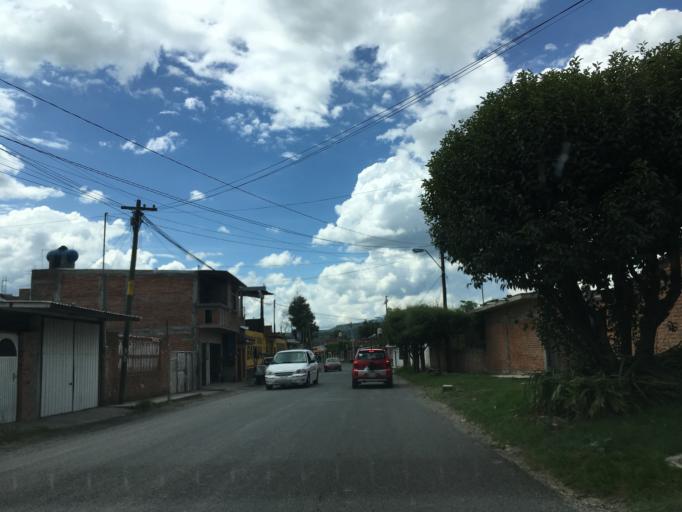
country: MX
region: Michoacan
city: Zacapu
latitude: 19.8370
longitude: -101.7636
